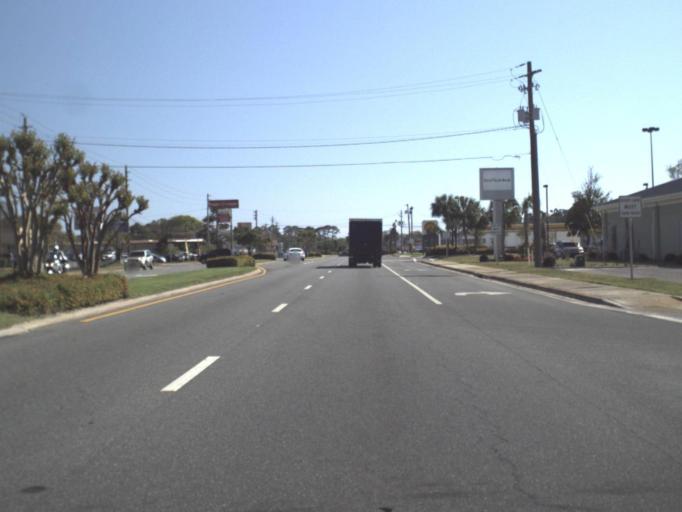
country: US
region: Florida
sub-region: Okaloosa County
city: Mary Esther
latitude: 30.4164
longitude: -86.6539
